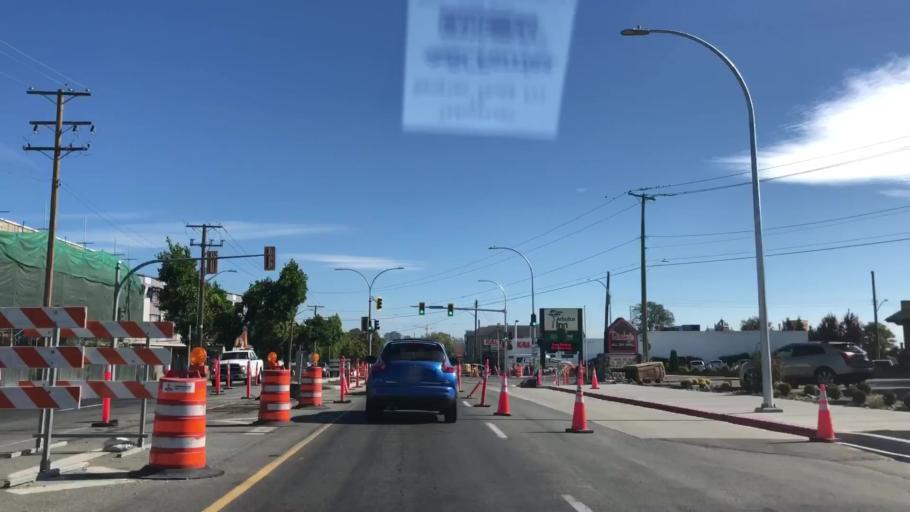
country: CA
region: British Columbia
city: Victoria
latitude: 48.4426
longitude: -123.3693
